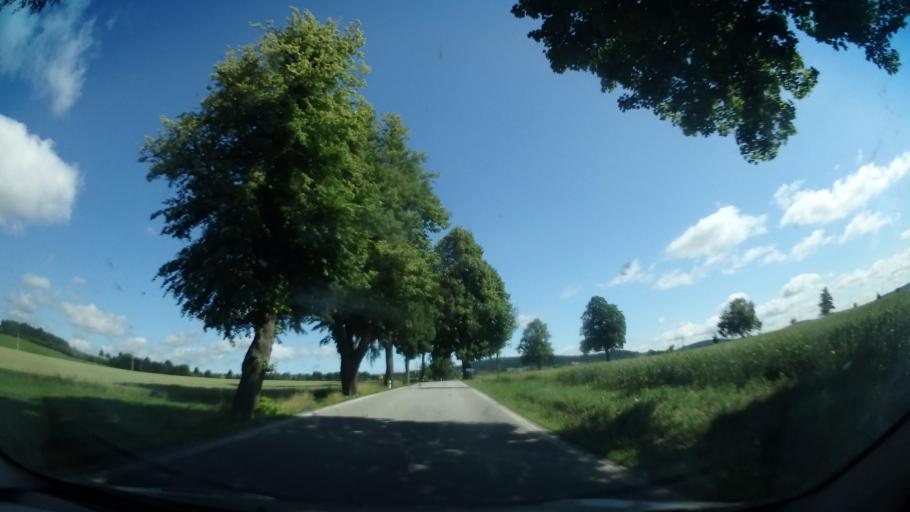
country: CZ
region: Vysocina
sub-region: Okres Zd'ar nad Sazavou
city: Nove Mesto na Morave
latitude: 49.6367
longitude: 16.1191
